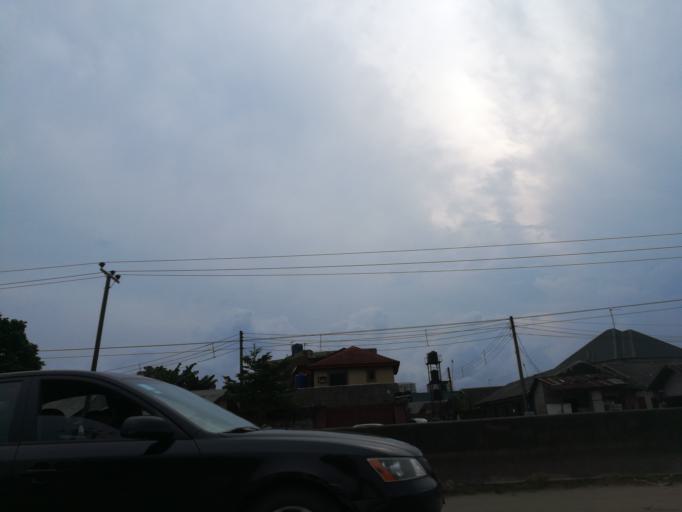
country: NG
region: Rivers
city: Okrika
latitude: 4.7829
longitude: 7.1207
